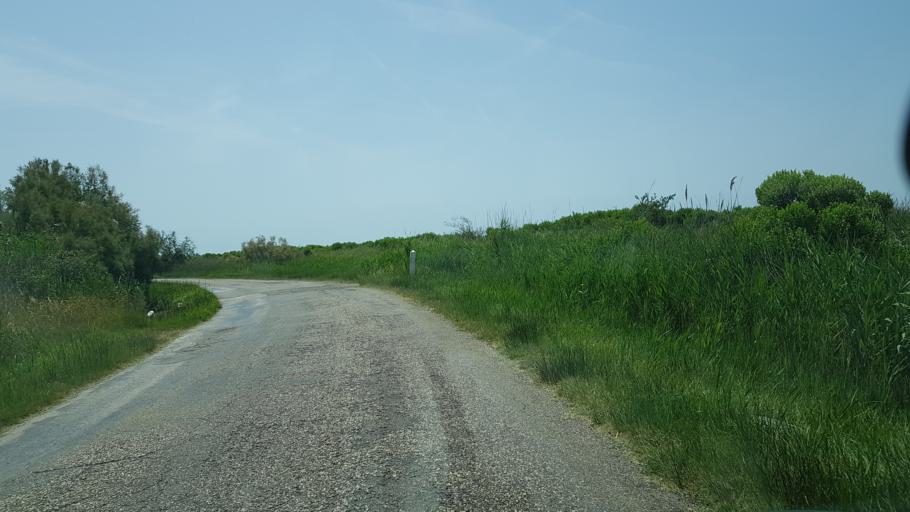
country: FR
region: Provence-Alpes-Cote d'Azur
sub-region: Departement des Bouches-du-Rhone
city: Arles
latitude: 43.5542
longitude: 4.6258
